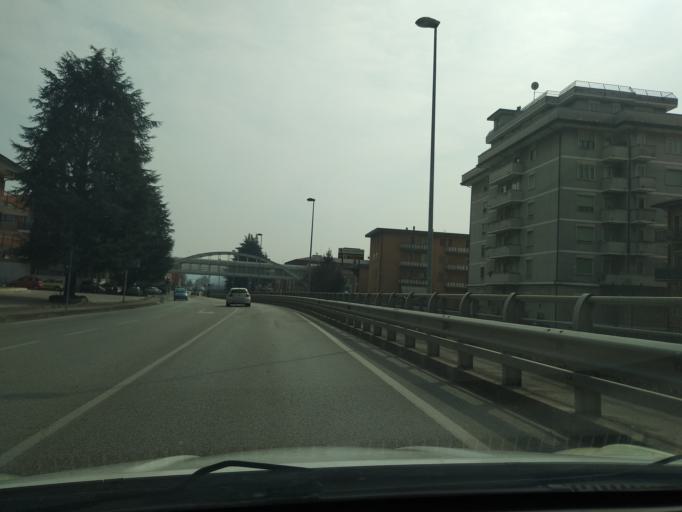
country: IT
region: Veneto
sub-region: Provincia di Vicenza
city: Chiampo
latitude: 45.5468
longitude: 11.2797
